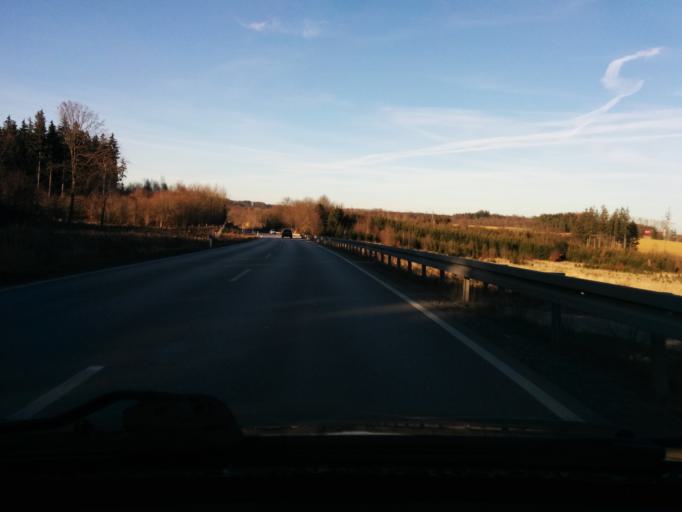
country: DE
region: Bavaria
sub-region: Upper Bavaria
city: Gilching
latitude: 48.0865
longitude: 11.3184
